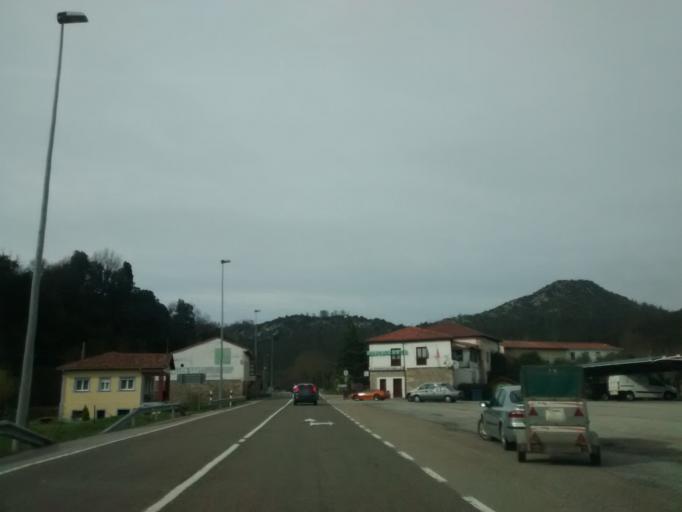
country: ES
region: Cantabria
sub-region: Provincia de Cantabria
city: Corvera
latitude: 43.2756
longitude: -3.9471
